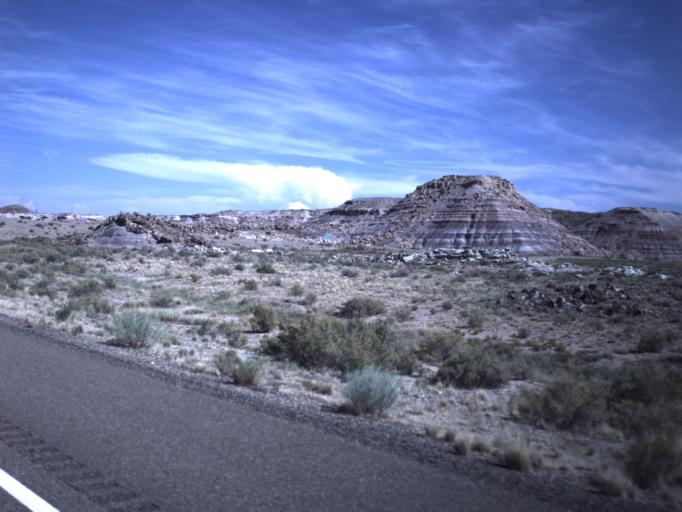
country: US
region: Utah
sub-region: Carbon County
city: East Carbon City
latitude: 38.9220
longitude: -110.3797
